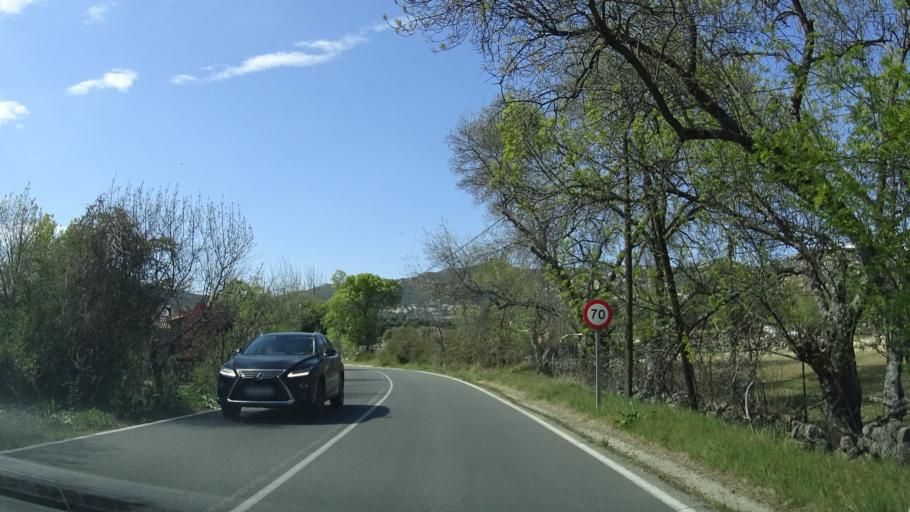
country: ES
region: Madrid
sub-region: Provincia de Madrid
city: Hoyo de Manzanares
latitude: 40.6233
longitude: -3.8967
